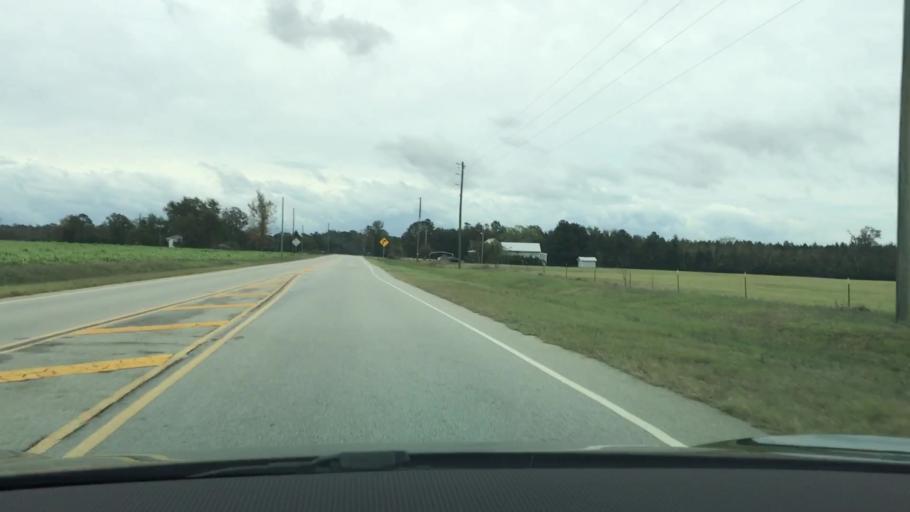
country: US
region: Georgia
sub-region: Jefferson County
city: Louisville
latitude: 33.1003
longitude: -82.4221
